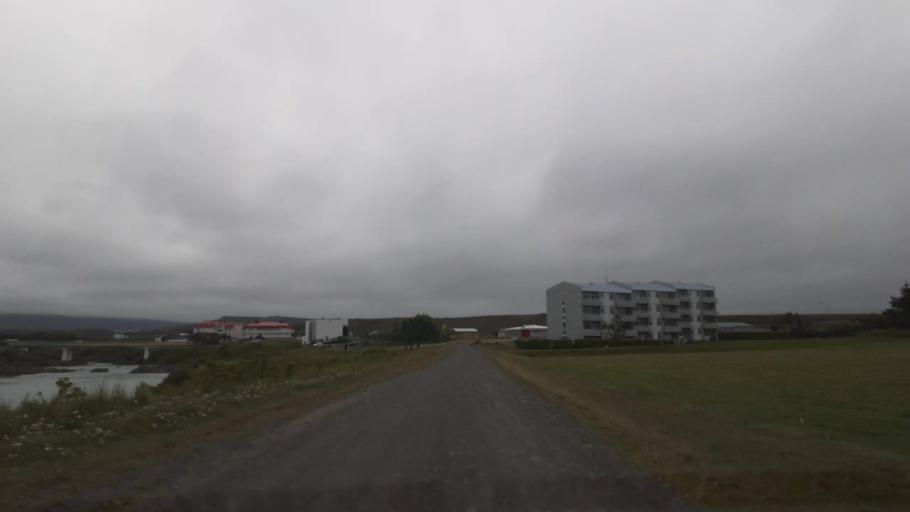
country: IS
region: Northwest
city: Saudarkrokur
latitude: 65.6587
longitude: -20.2906
